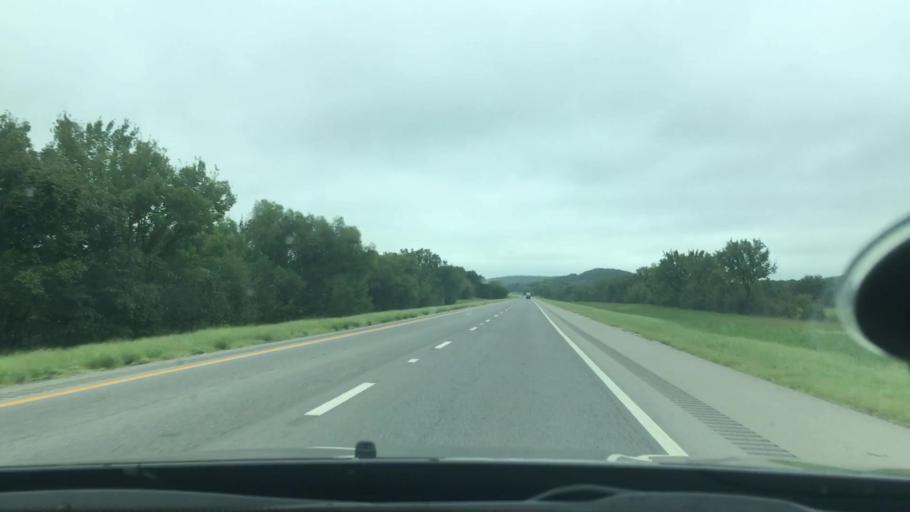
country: US
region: Oklahoma
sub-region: McIntosh County
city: Checotah
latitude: 35.4567
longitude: -95.4151
